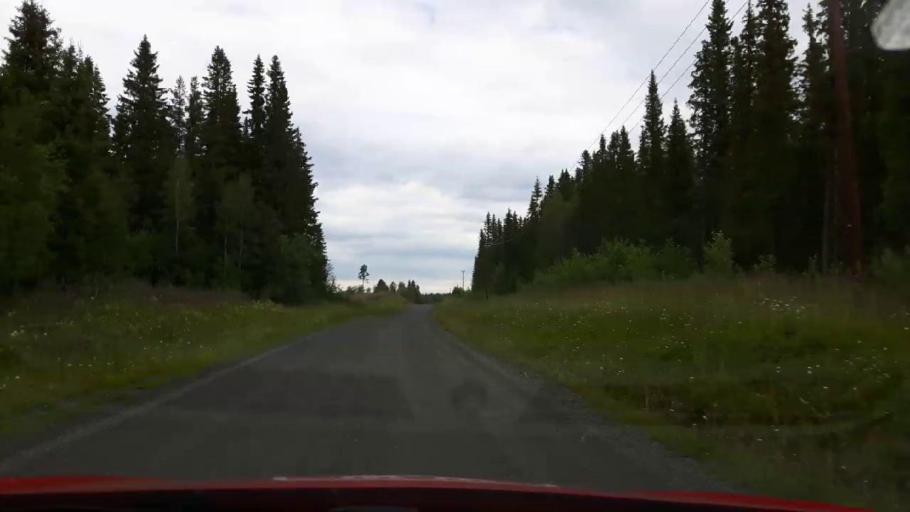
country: SE
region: Jaemtland
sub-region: Stroemsunds Kommun
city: Stroemsund
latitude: 63.4832
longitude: 15.3053
